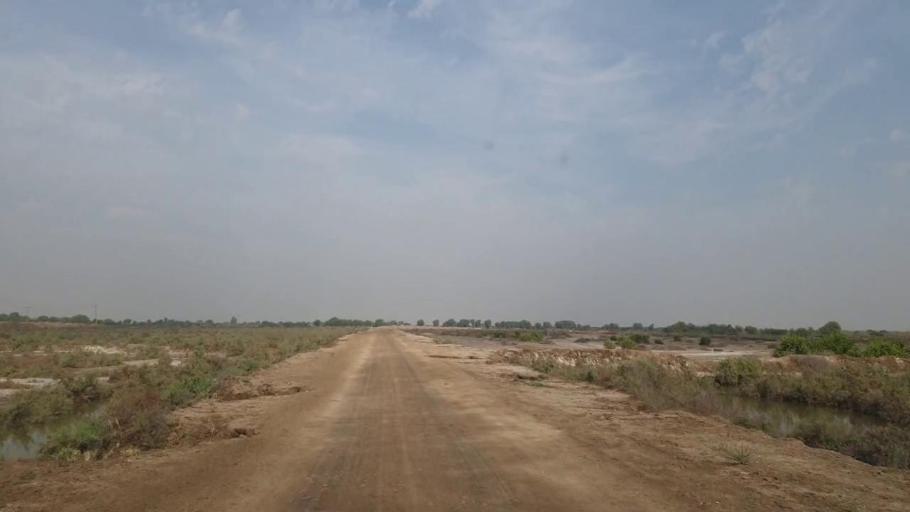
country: PK
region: Sindh
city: Rajo Khanani
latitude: 24.9943
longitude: 68.9952
